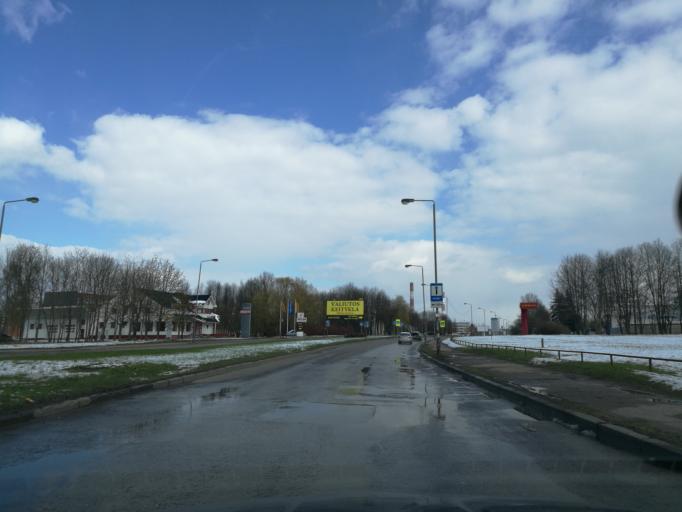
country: LT
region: Kauno apskritis
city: Dainava (Kaunas)
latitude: 54.9185
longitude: 23.9901
